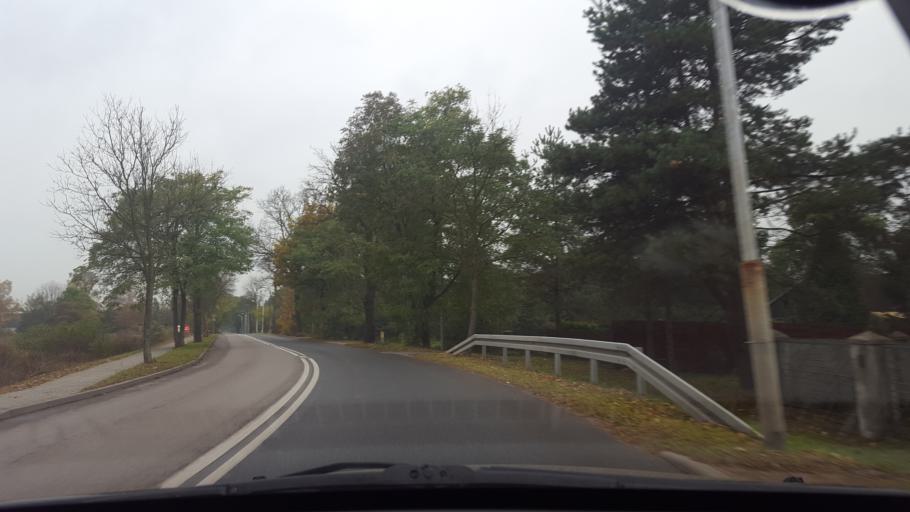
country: PL
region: Silesian Voivodeship
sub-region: Ruda Slaska
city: Ruda Slaska
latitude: 50.2367
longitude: 18.8553
